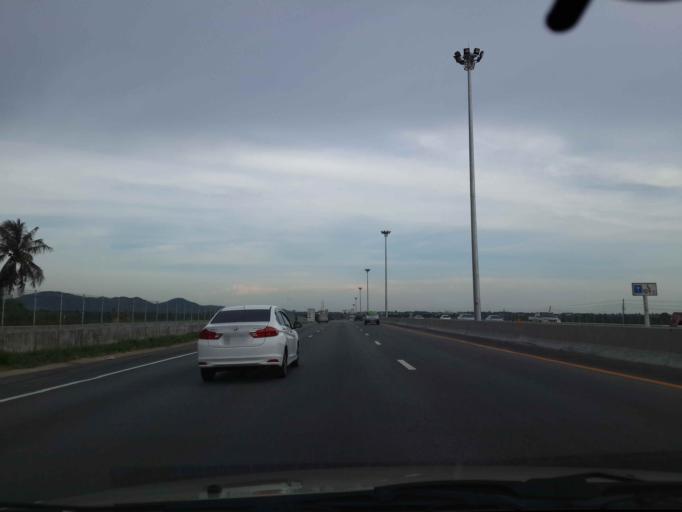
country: TH
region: Chon Buri
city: Ban Talat Bueng
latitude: 13.0323
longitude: 100.9964
